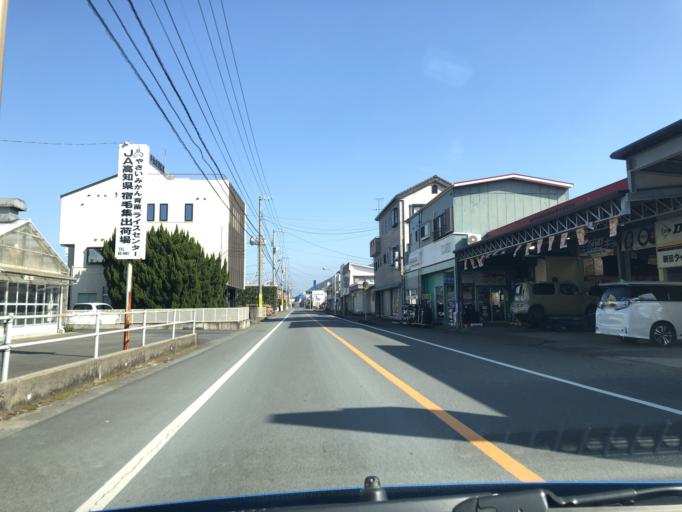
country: JP
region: Kochi
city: Sukumo
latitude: 32.9277
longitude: 132.7098
